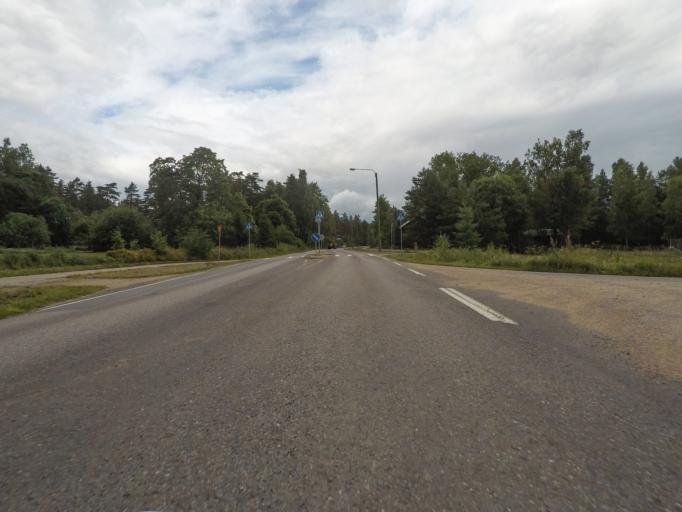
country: FI
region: Varsinais-Suomi
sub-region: Salo
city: Muurla
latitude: 60.3642
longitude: 23.2980
